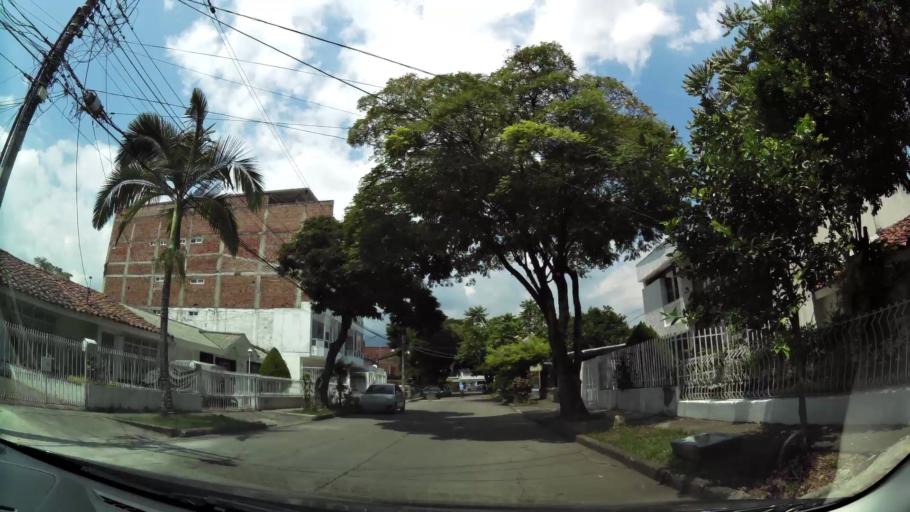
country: CO
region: Valle del Cauca
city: Cali
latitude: 3.4031
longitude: -76.5390
